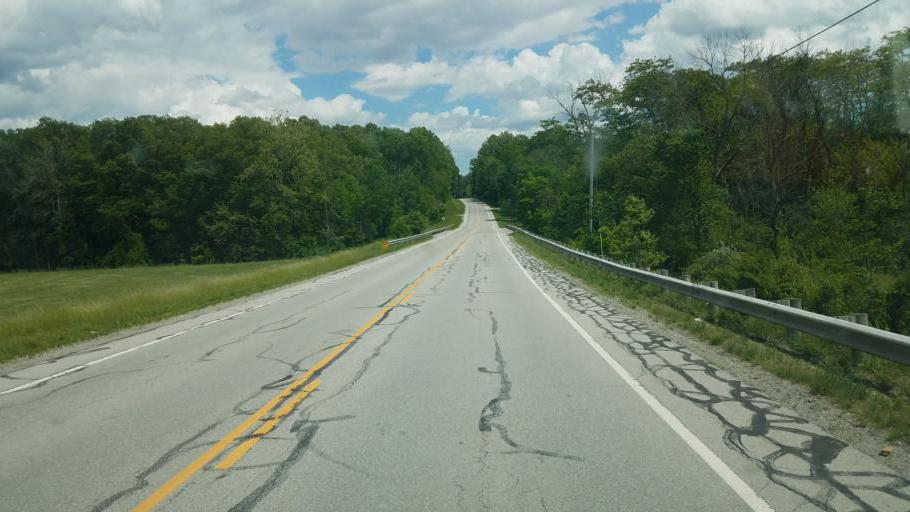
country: US
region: Ohio
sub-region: Crawford County
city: Galion
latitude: 40.8071
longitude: -82.8123
